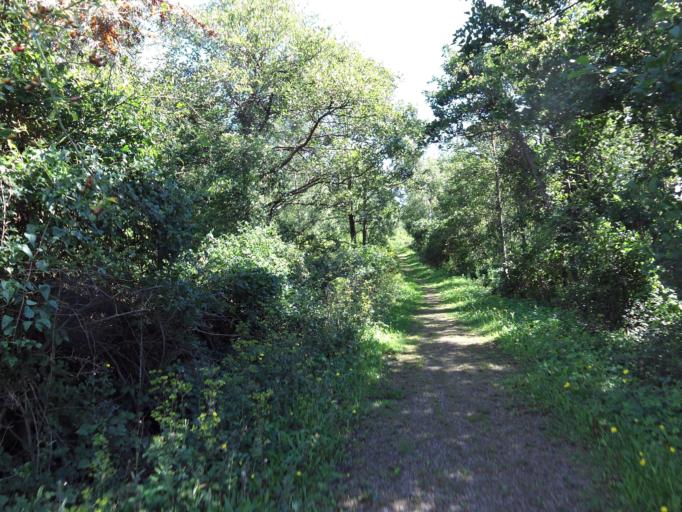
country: DE
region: North Rhine-Westphalia
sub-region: Regierungsbezirk Koln
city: Herzogenrath
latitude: 50.8916
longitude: 6.1102
